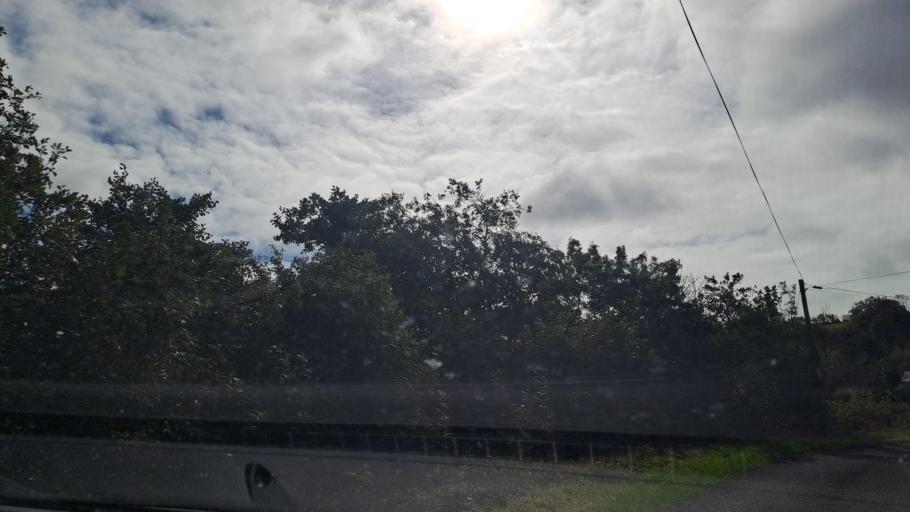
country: IE
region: Ulster
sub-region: An Cabhan
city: Kingscourt
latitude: 53.9739
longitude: -6.8677
